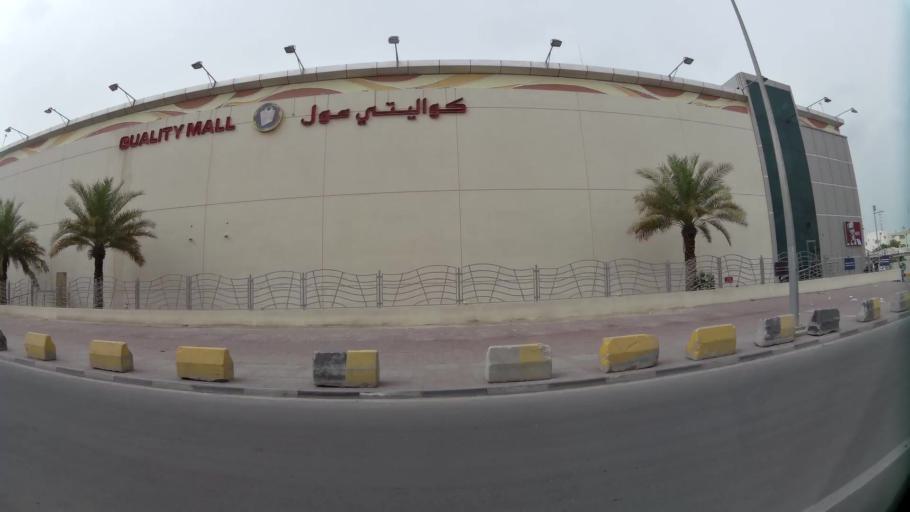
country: QA
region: Baladiyat ad Dawhah
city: Doha
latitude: 25.2516
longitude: 51.5156
